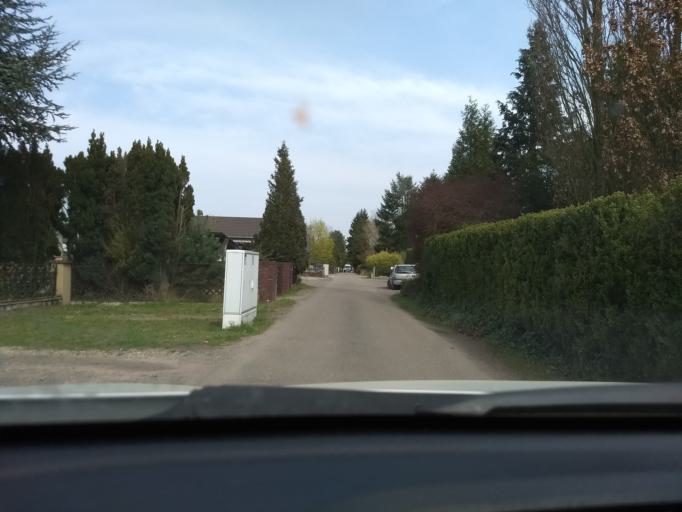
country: DE
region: Rheinland-Pfalz
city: Hanhofen
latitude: 49.3494
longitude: 8.3265
